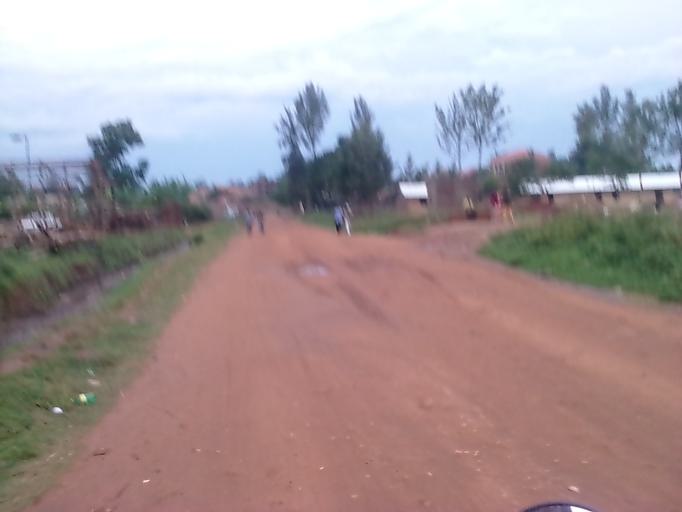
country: UG
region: Eastern Region
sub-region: Mbale District
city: Mbale
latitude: 1.0755
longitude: 34.1666
